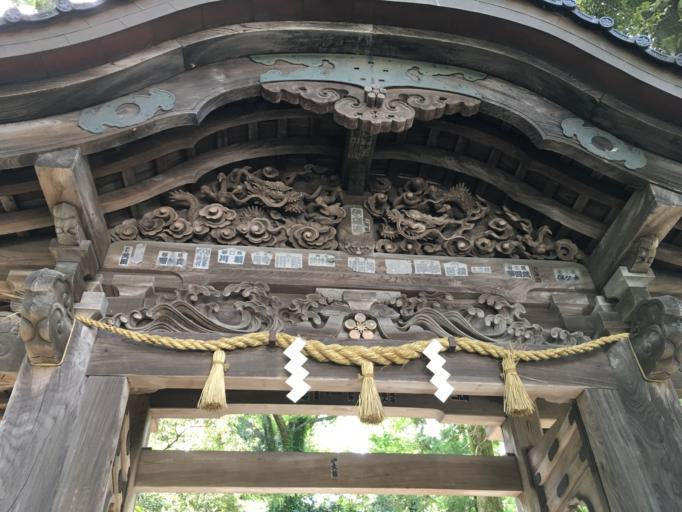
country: JP
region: Ishikawa
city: Kanazawa-shi
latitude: 36.5654
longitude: 136.6562
